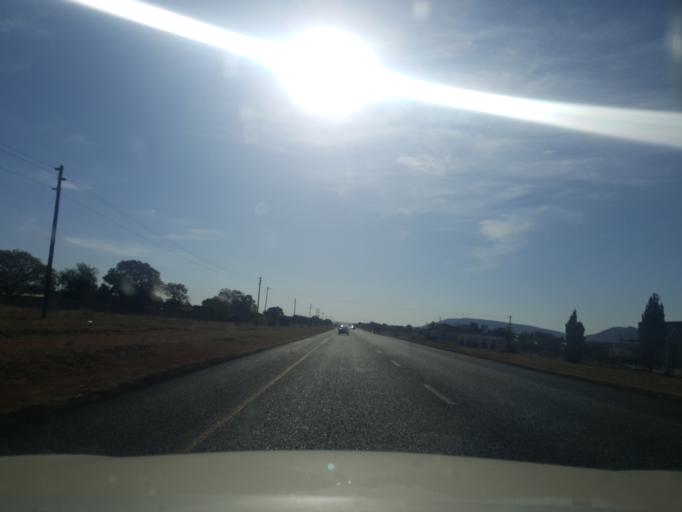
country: ZA
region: North-West
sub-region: Ngaka Modiri Molema District Municipality
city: Zeerust
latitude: -25.4834
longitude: 25.9149
